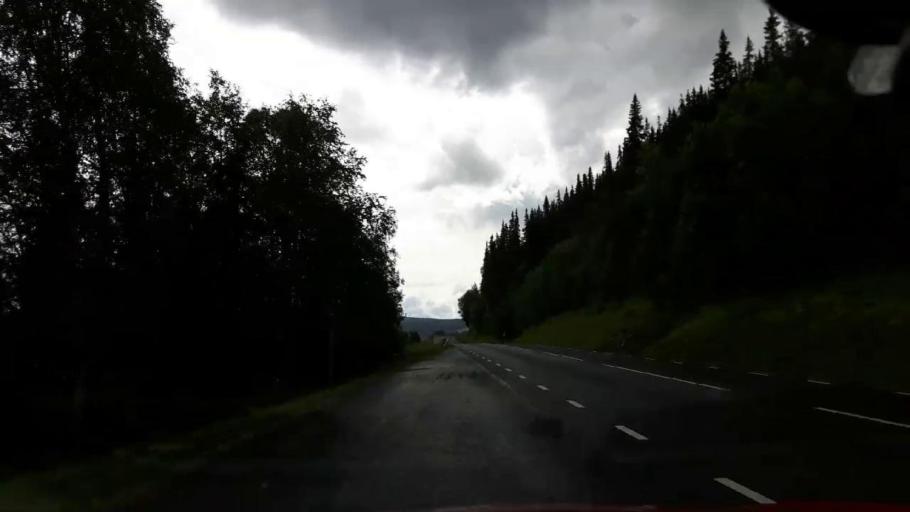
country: NO
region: Nord-Trondelag
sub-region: Royrvik
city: Royrvik
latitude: 64.8283
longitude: 14.0792
